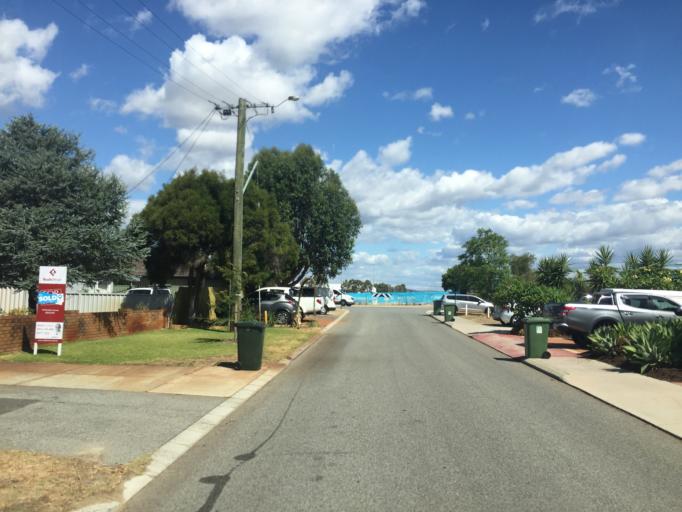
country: AU
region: Western Australia
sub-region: Belmont
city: Redcliffe
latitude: -31.9346
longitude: 115.9472
